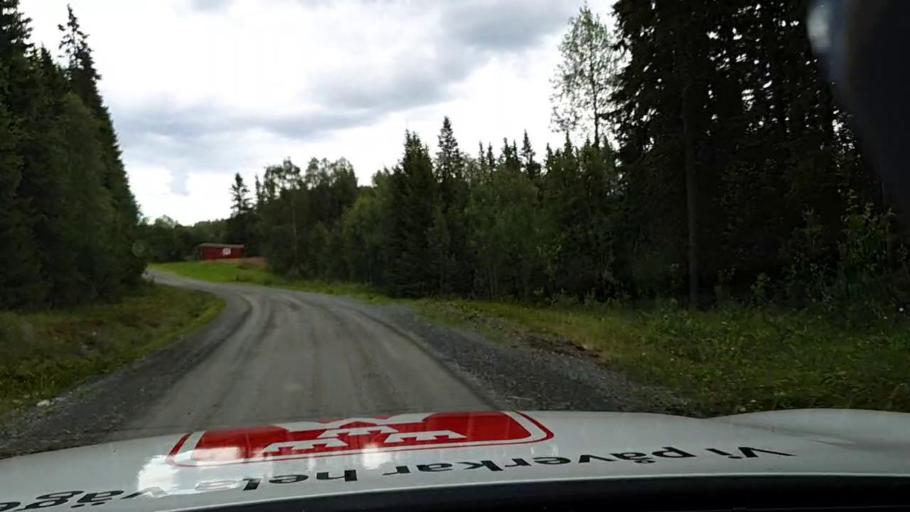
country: SE
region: Jaemtland
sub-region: Krokoms Kommun
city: Valla
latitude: 63.5319
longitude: 13.9102
